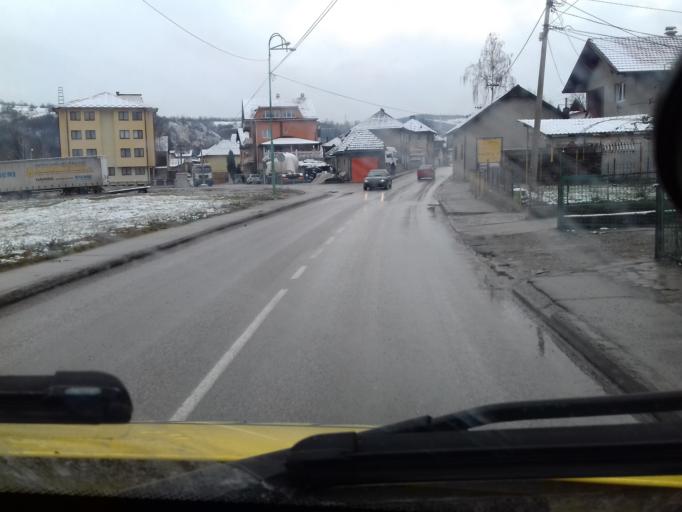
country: BA
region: Federation of Bosnia and Herzegovina
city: Kakanj
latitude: 44.1178
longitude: 18.1161
